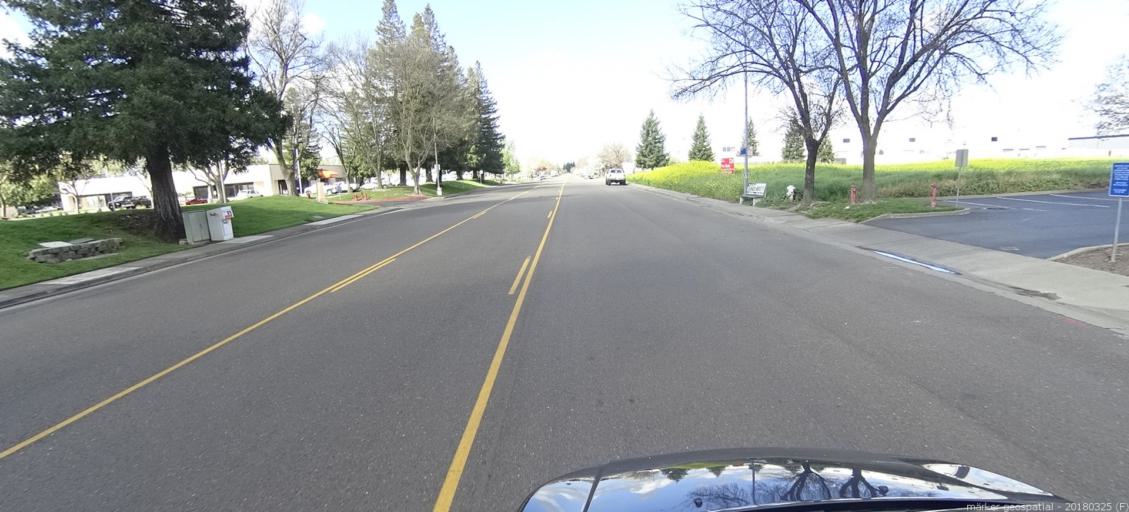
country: US
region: California
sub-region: Sacramento County
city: Sacramento
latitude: 38.6435
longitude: -121.4920
